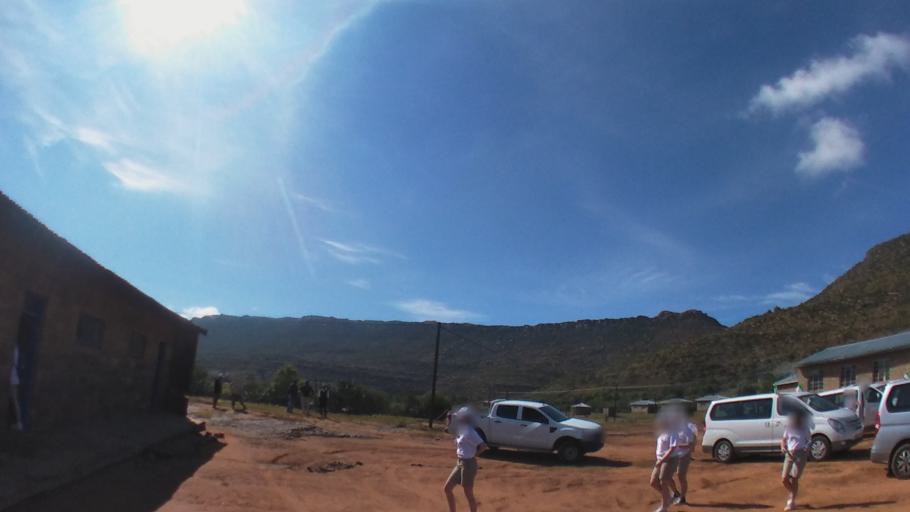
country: LS
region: Maseru
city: Maseru
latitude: -29.4414
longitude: 27.4129
